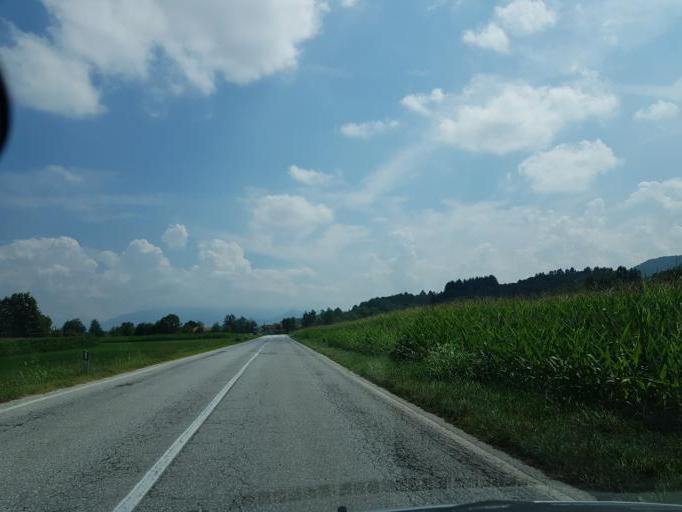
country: IT
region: Piedmont
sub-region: Provincia di Cuneo
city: Cervasca
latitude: 44.3891
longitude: 7.4603
